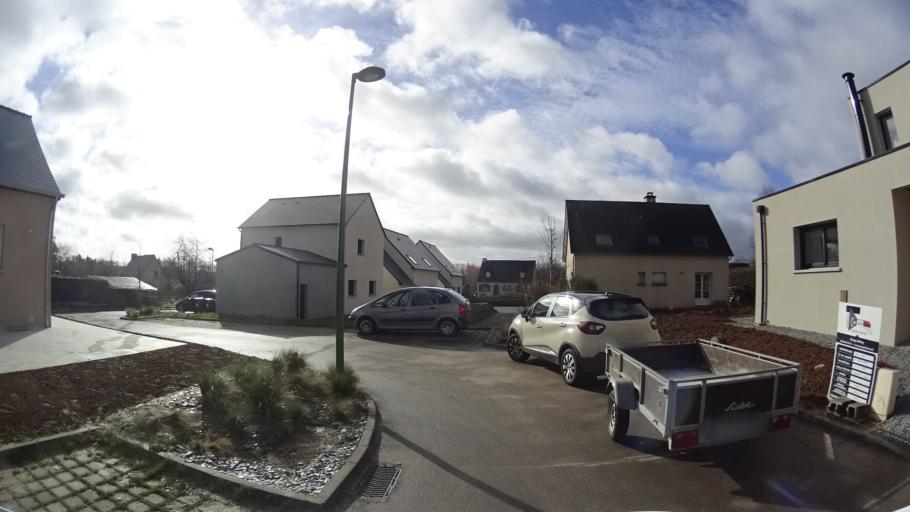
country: FR
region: Brittany
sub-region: Departement d'Ille-et-Vilaine
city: Romille
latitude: 48.2159
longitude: -1.9011
